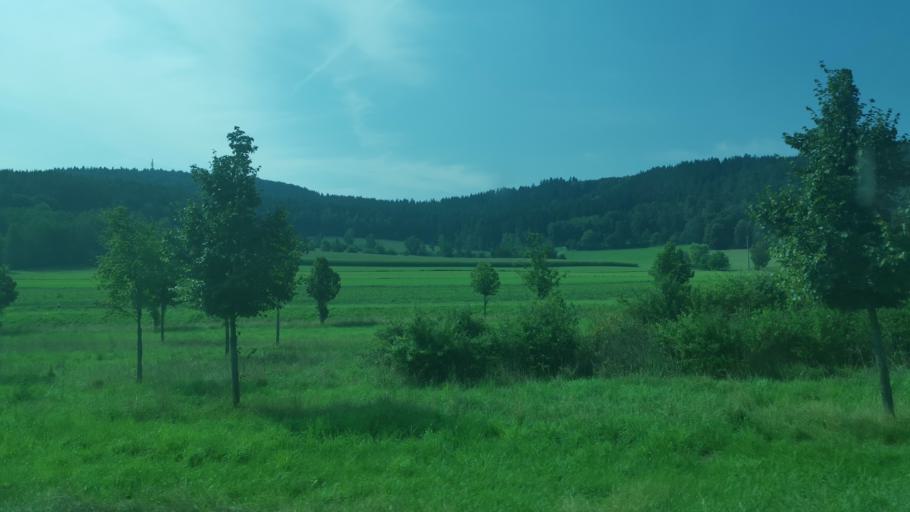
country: DE
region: Bavaria
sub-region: Upper Palatinate
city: Chamerau
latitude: 49.2114
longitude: 12.7161
